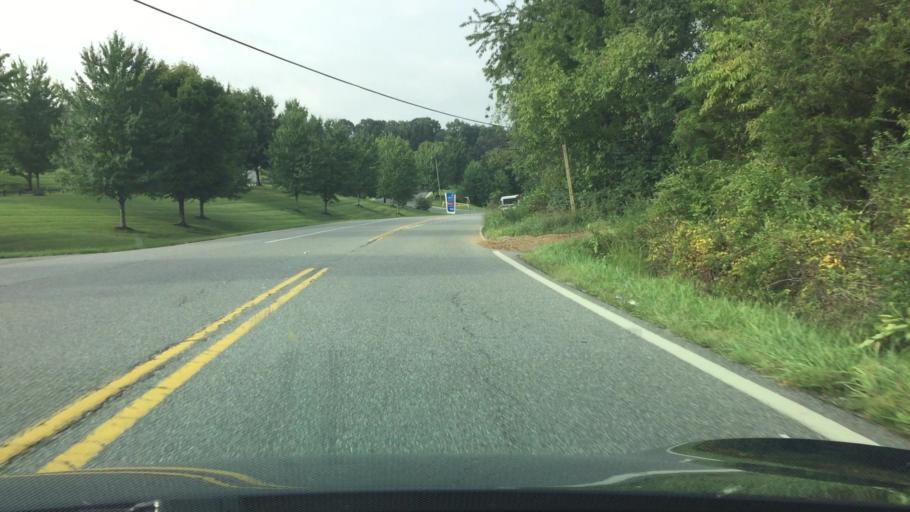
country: US
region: Virginia
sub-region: City of Radford
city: Radford
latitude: 37.0908
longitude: -80.5066
